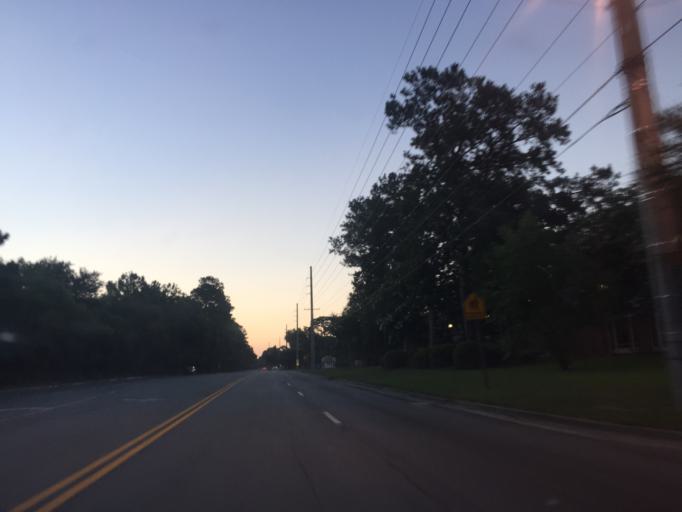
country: US
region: Georgia
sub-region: Chatham County
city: Isle of Hope
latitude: 31.9929
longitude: -81.1007
